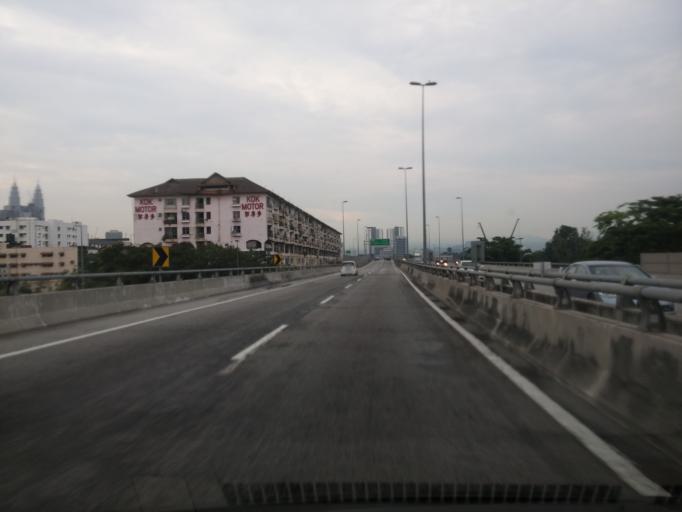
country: MY
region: Kuala Lumpur
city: Kuala Lumpur
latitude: 3.1318
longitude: 101.7184
